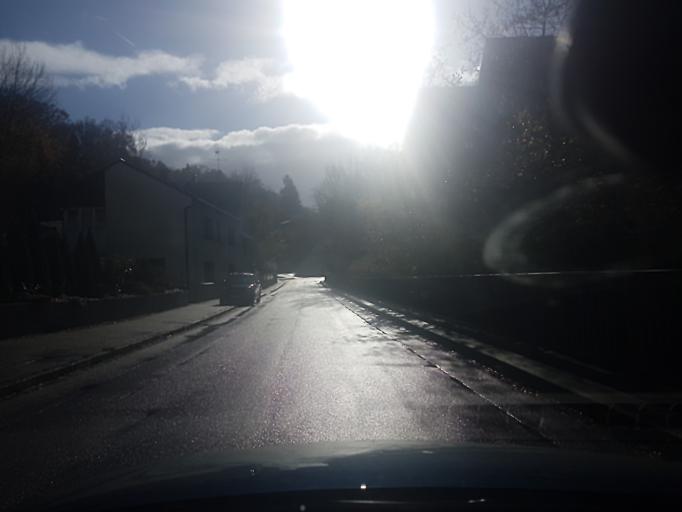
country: DE
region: Bavaria
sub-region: Lower Bavaria
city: Dingolfing
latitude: 48.6254
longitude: 12.4953
